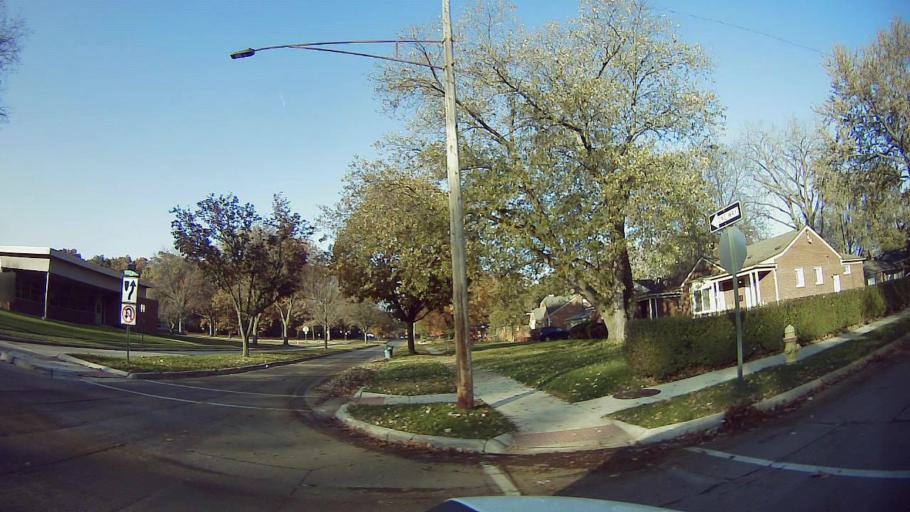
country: US
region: Michigan
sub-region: Oakland County
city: Huntington Woods
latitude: 42.4643
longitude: -83.1622
